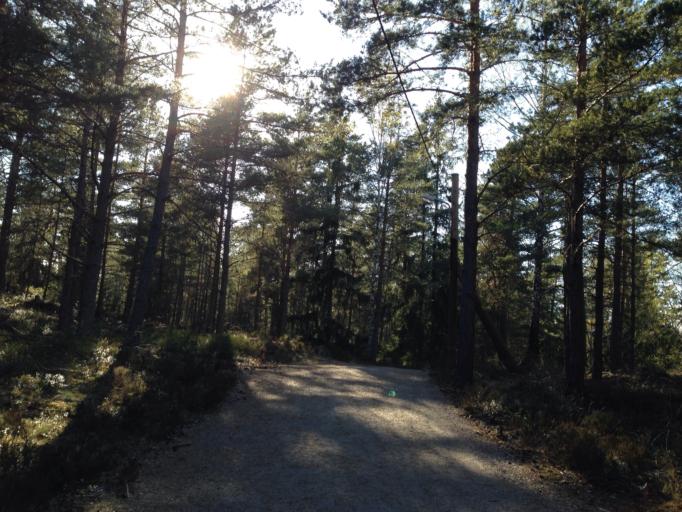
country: SE
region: Stockholm
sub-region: Nacka Kommun
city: Nacka
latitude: 59.2920
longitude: 18.1283
